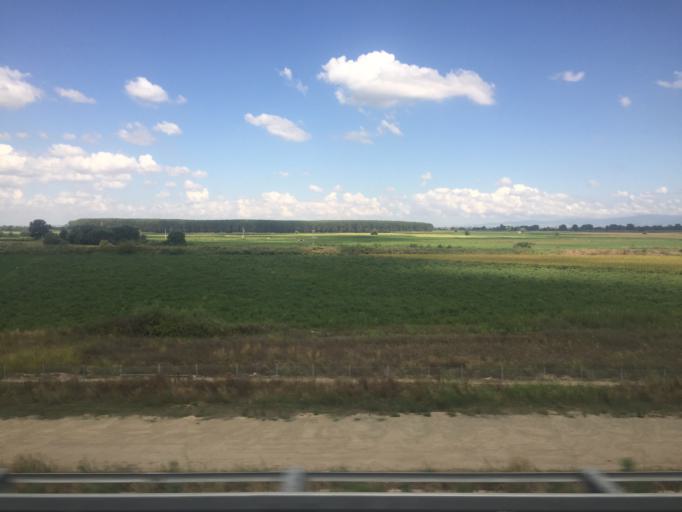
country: TR
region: Bursa
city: Tatkavakli
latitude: 40.0879
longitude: 28.2682
